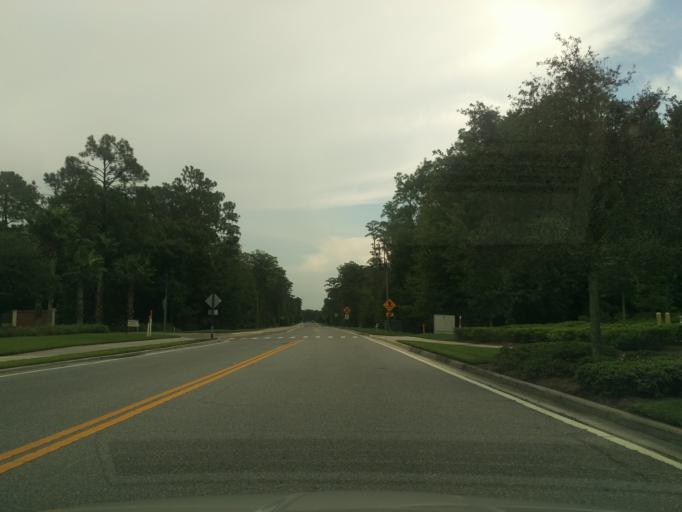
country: US
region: Florida
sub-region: Osceola County
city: Celebration
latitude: 28.3571
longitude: -81.5345
